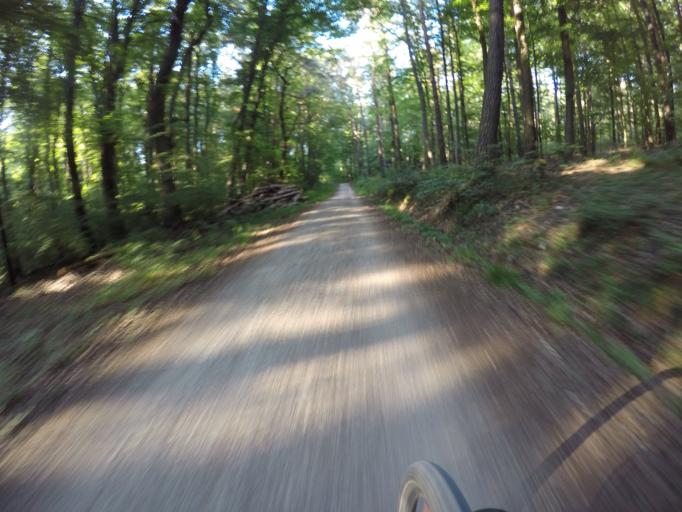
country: DE
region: Baden-Wuerttemberg
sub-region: Regierungsbezirk Stuttgart
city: Esslingen
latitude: 48.7762
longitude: 9.3149
